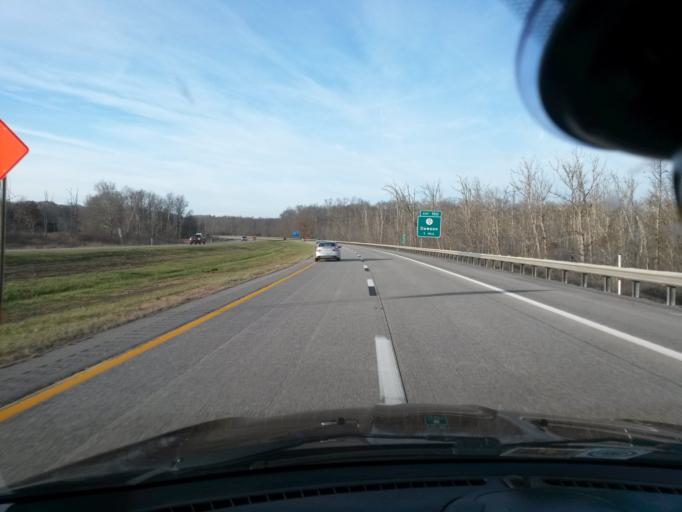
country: US
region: West Virginia
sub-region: Greenbrier County
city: Rainelle
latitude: 37.8666
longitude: -80.7076
